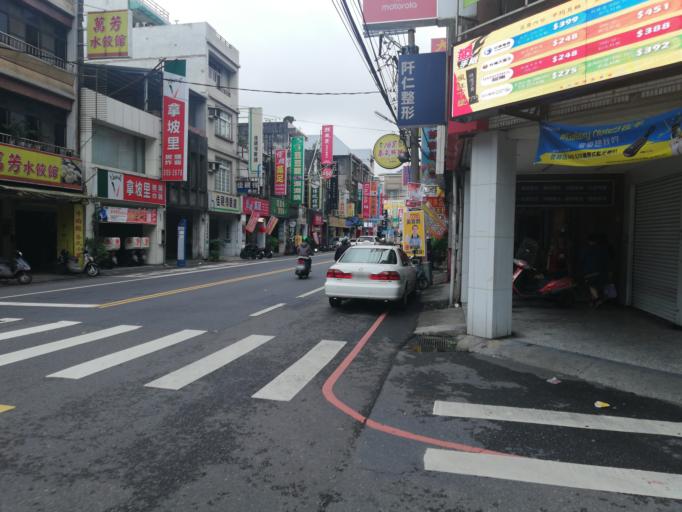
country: TW
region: Taiwan
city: Taoyuan City
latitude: 25.0047
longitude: 121.3047
